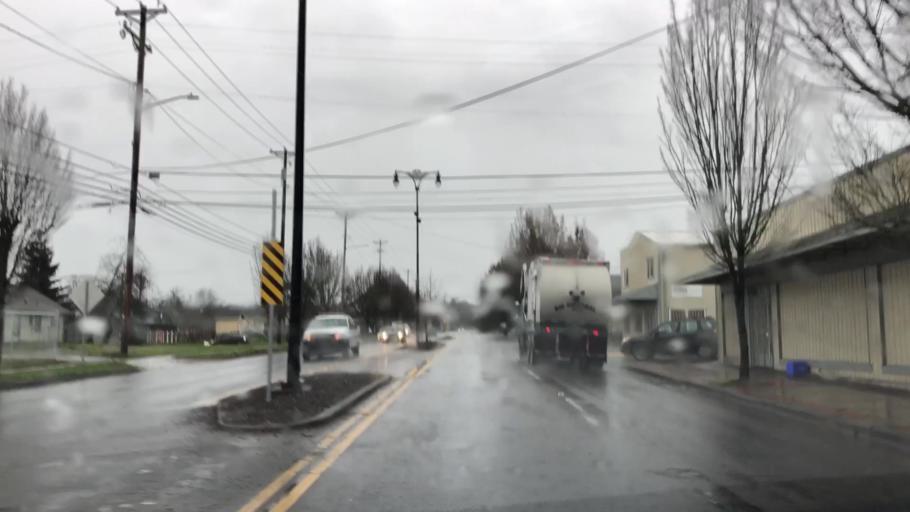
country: US
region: Washington
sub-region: Pierce County
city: Tacoma
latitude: 47.2345
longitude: -122.4095
